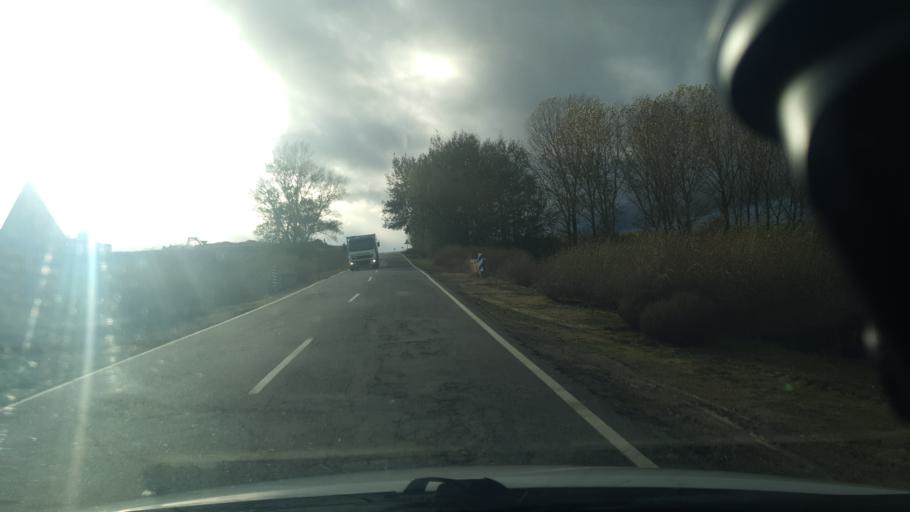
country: ES
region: Castille and Leon
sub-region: Provincia de Segovia
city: San Cristobal de la Vega
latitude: 41.1184
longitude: -4.6243
